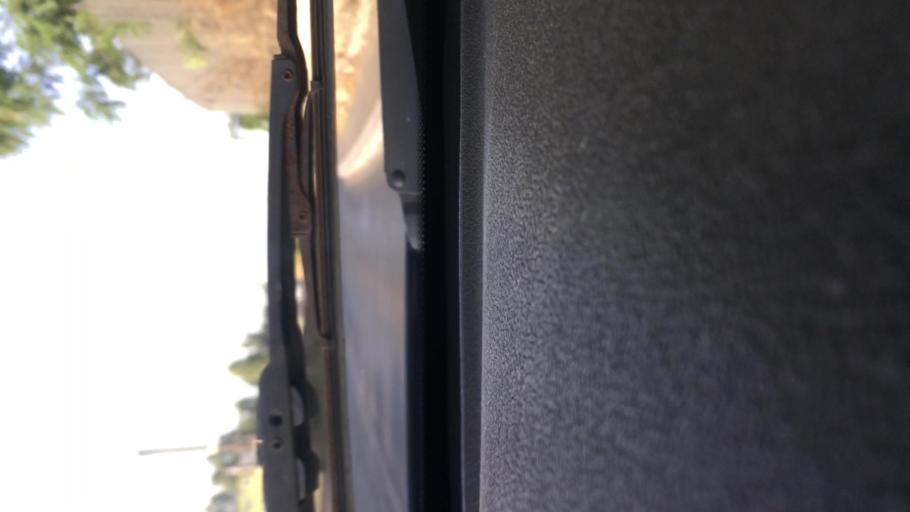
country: IT
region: Latium
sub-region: Citta metropolitana di Roma Capitale
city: Borgo Lotti
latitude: 41.8005
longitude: 12.5363
